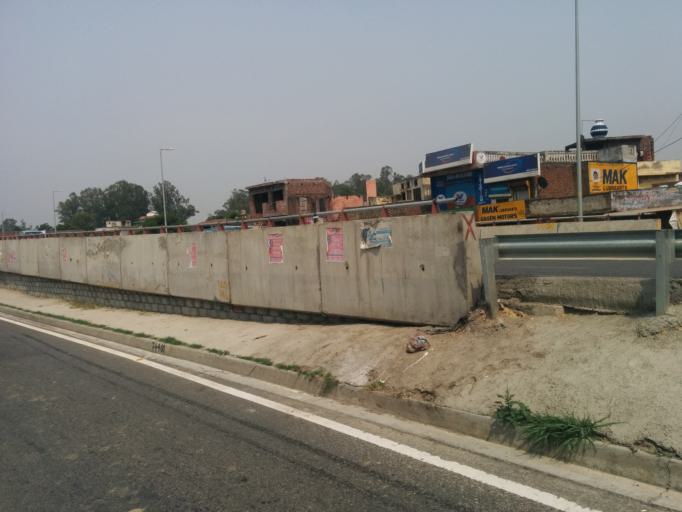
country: IN
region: Punjab
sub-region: Pathankot
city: Pathankot
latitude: 32.2608
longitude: 75.5852
